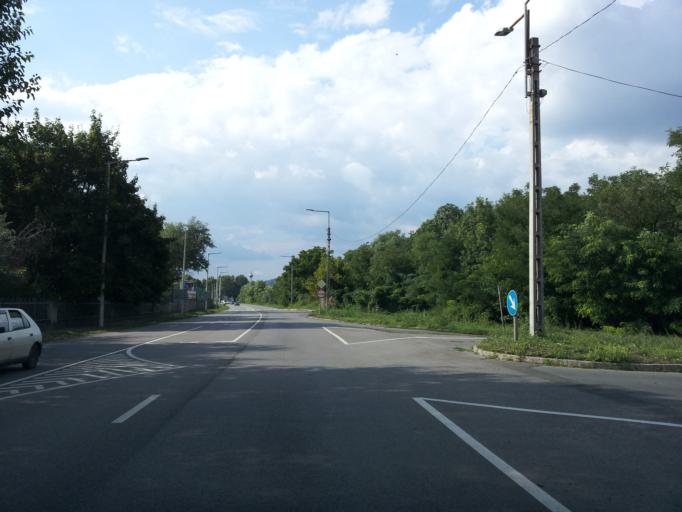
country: HU
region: Pest
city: Vac
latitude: 47.7951
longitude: 19.1129
